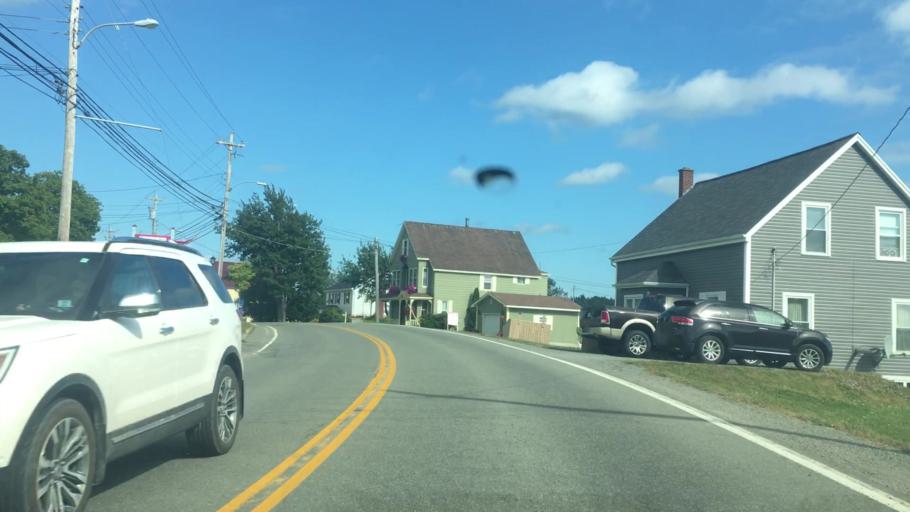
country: CA
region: Nova Scotia
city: Princeville
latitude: 45.6552
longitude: -60.8790
